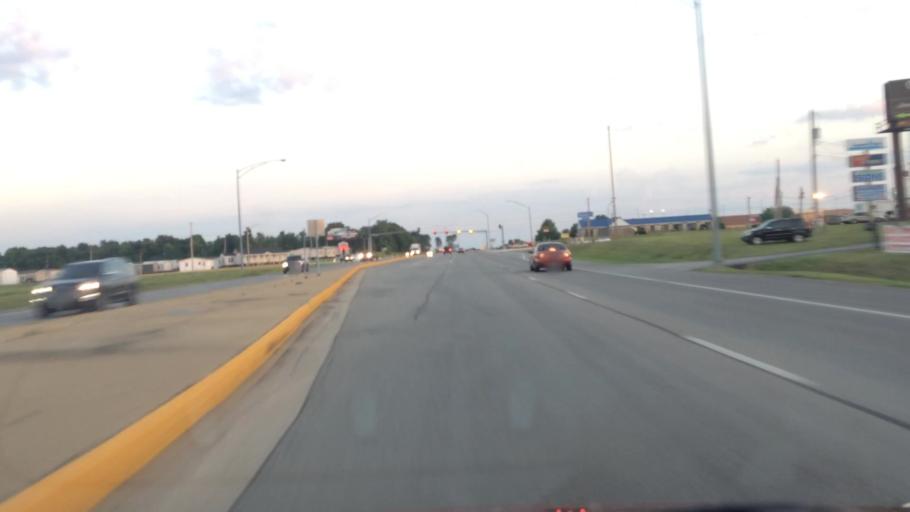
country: US
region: Missouri
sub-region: Greene County
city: Springfield
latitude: 37.1852
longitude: -93.3504
